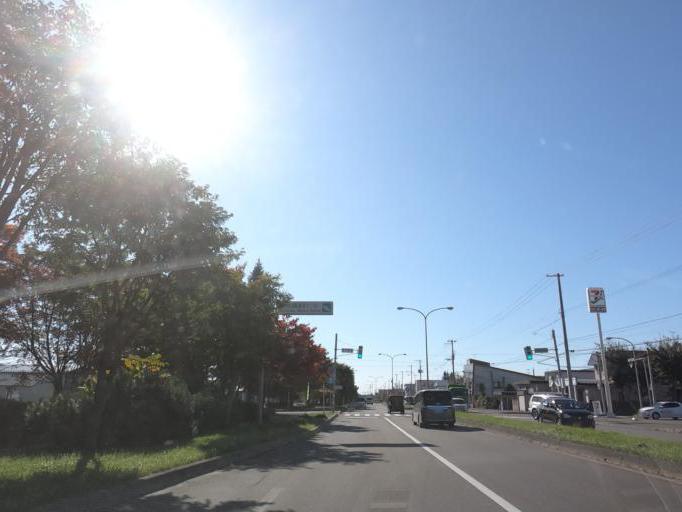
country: JP
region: Hokkaido
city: Obihiro
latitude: 42.9095
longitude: 143.2140
